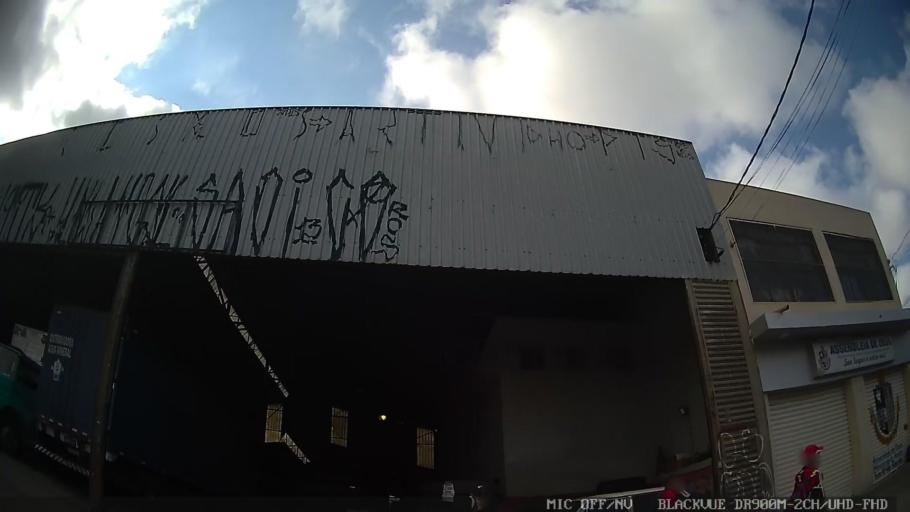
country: BR
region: Sao Paulo
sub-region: Sao Caetano Do Sul
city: Sao Caetano do Sul
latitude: -23.5577
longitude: -46.5205
